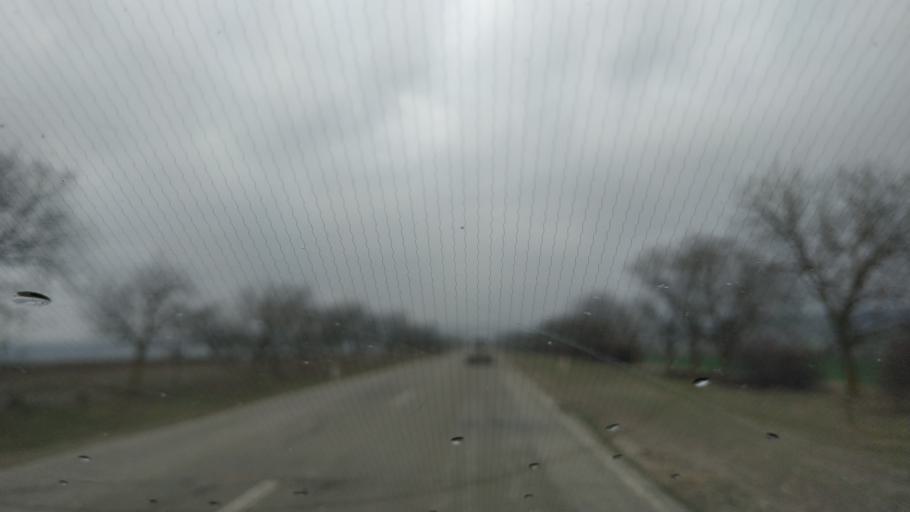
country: MD
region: Gagauzia
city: Comrat
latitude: 46.2506
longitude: 28.7581
